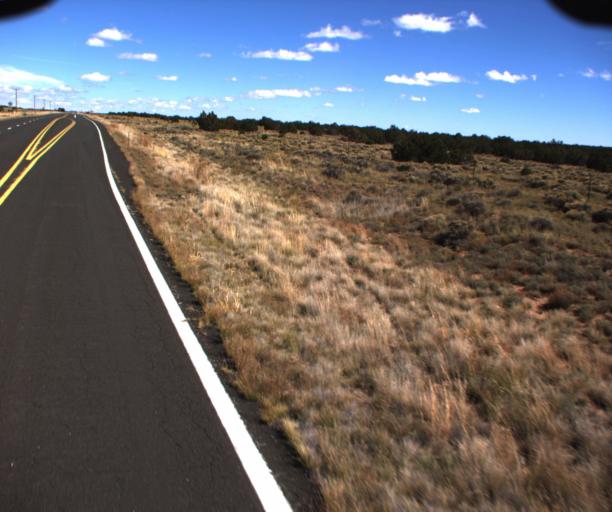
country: US
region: New Mexico
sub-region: McKinley County
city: Zuni Pueblo
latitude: 34.9641
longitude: -109.1518
